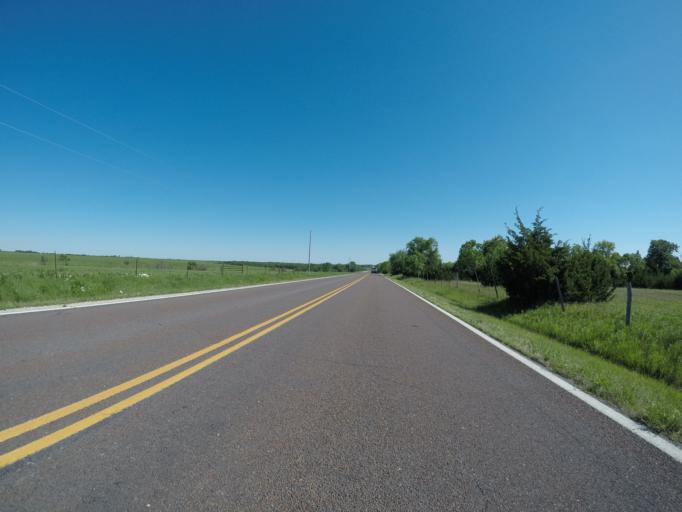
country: US
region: Kansas
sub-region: Osage County
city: Osage City
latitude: 38.7039
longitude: -96.0939
